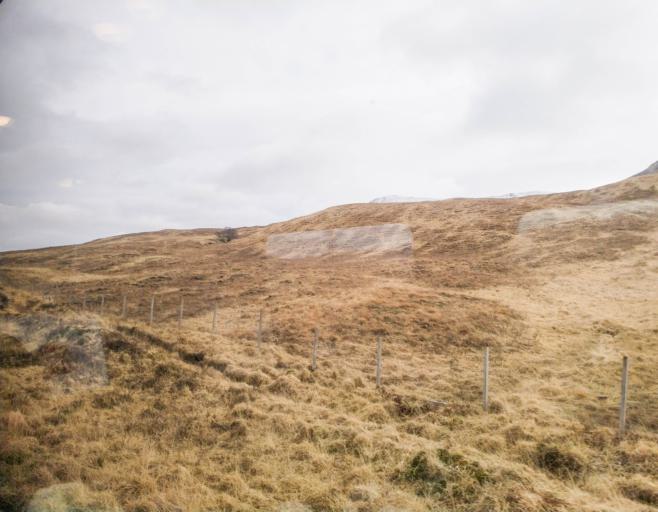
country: GB
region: Scotland
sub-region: Highland
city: Spean Bridge
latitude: 56.5403
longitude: -4.7595
